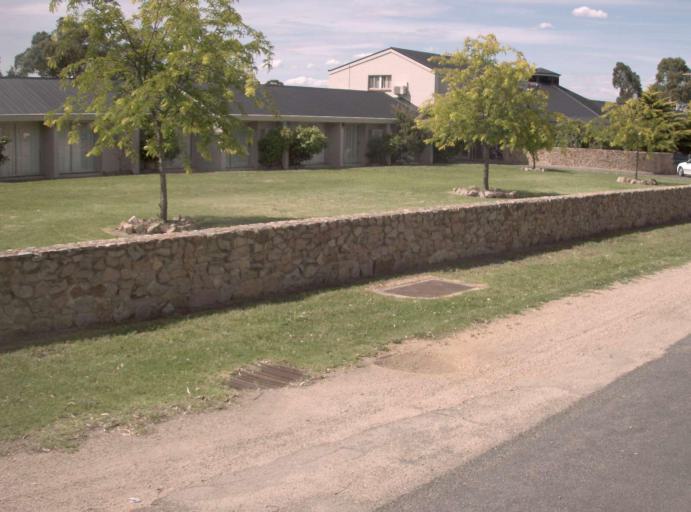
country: AU
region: Victoria
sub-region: East Gippsland
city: Bairnsdale
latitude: -37.8371
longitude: 147.5983
